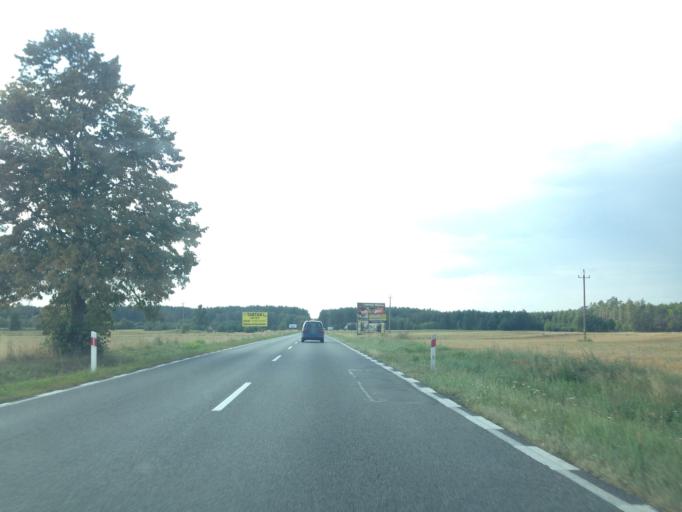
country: PL
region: Kujawsko-Pomorskie
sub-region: Powiat swiecki
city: Swiekatowo
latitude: 53.4785
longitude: 18.1436
